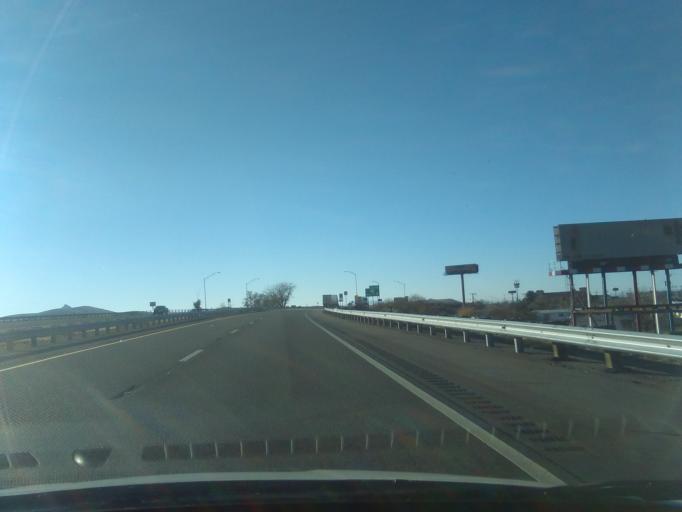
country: US
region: New Mexico
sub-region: Hidalgo County
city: Lordsburg
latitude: 32.3414
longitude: -108.7068
